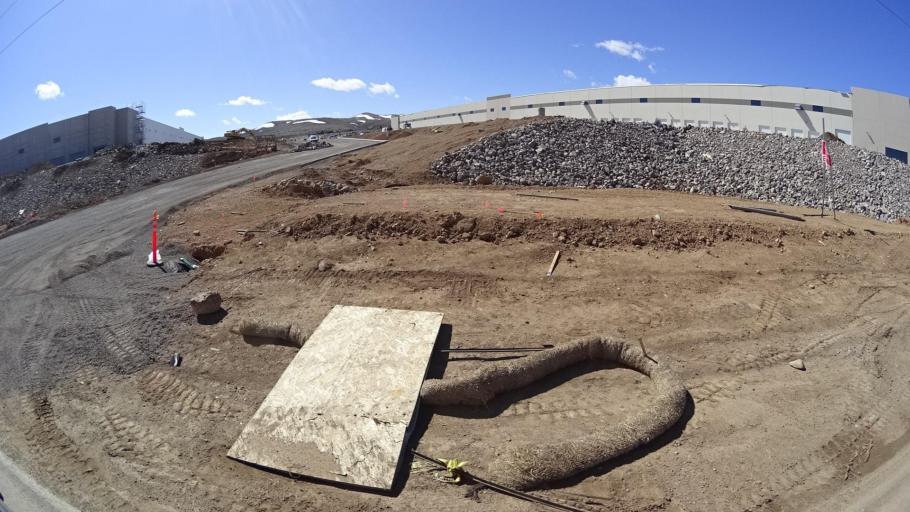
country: US
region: Nevada
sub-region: Washoe County
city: Lemmon Valley
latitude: 39.6072
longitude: -119.8614
